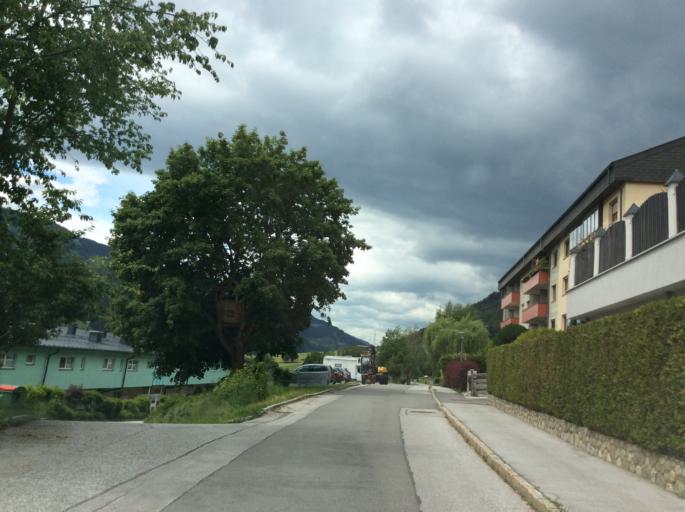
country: AT
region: Styria
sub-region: Politischer Bezirk Liezen
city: Schladming
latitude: 47.3973
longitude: 13.6827
